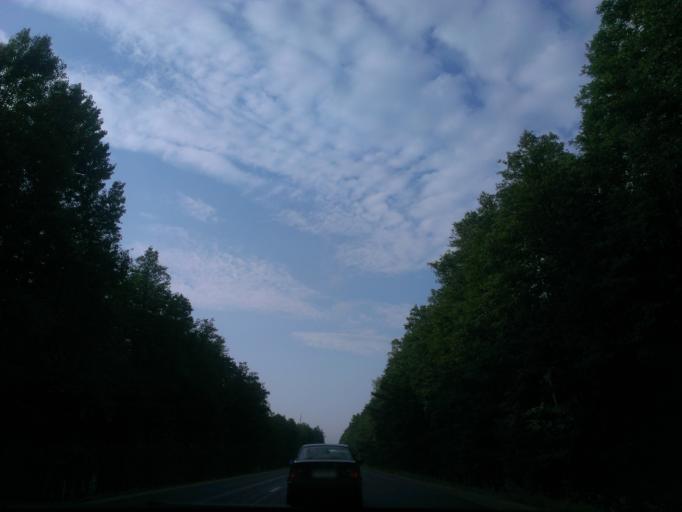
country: LV
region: Kekava
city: Kekava
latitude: 56.7394
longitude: 24.2524
